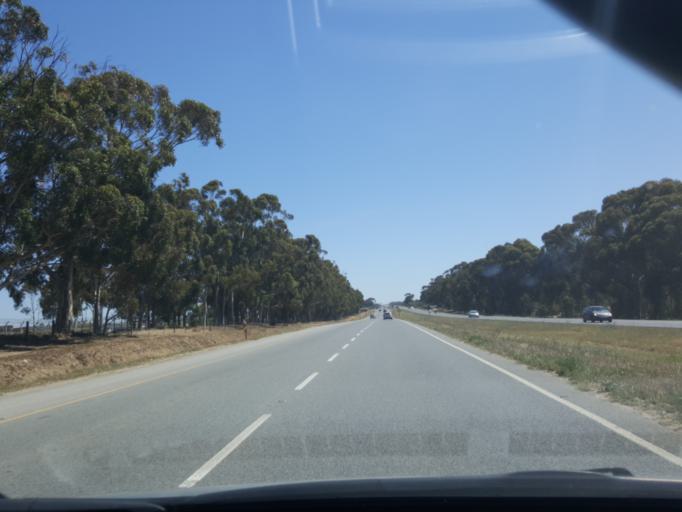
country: ZA
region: Western Cape
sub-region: City of Cape Town
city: Sunset Beach
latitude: -33.7742
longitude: 18.5483
